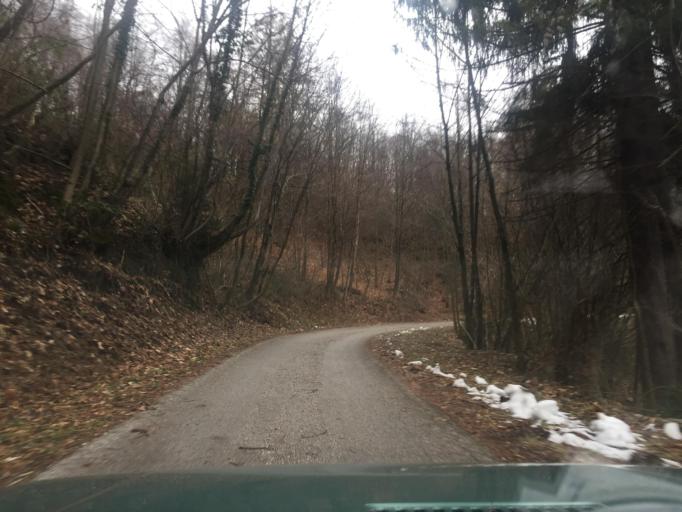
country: SI
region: Kanal
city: Kanal
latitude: 46.0756
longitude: 13.6711
